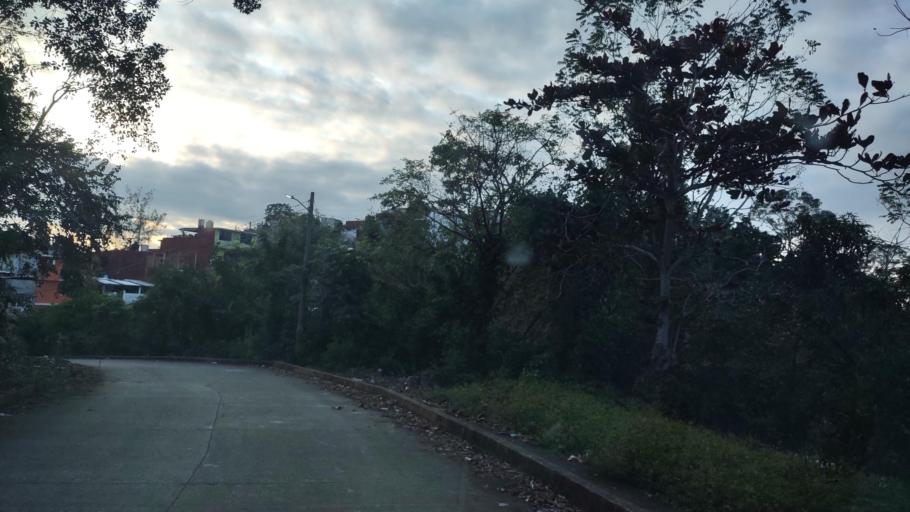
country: MX
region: Veracruz
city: Papantla de Olarte
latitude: 20.4559
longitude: -97.3060
